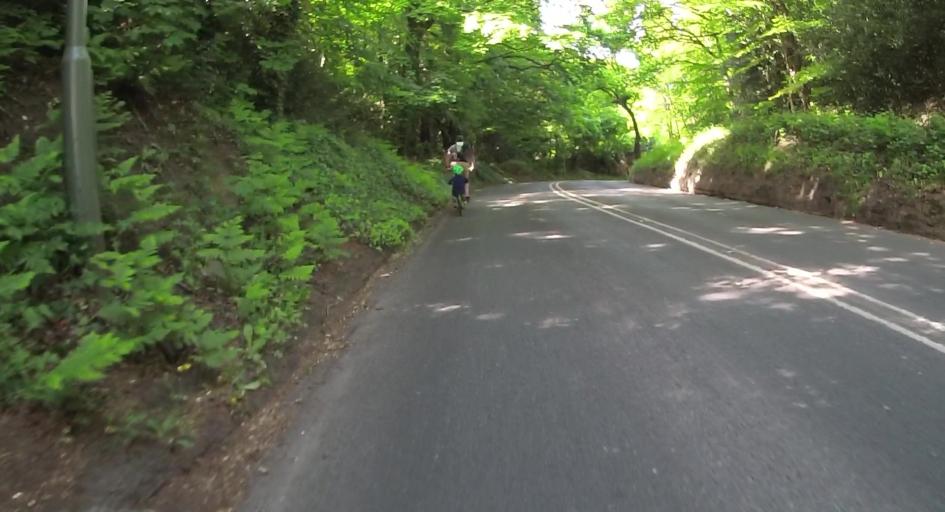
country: GB
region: England
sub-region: Surrey
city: Hale
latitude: 51.2404
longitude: -0.7871
